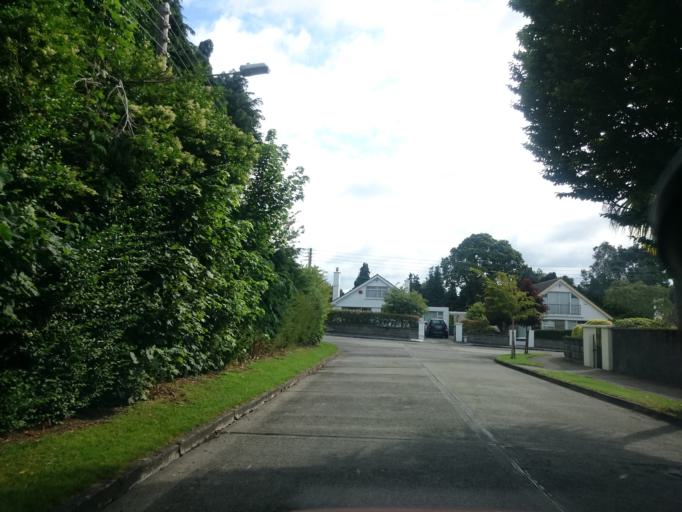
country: IE
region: Leinster
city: Mount Merrion
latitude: 53.2913
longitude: -6.2075
